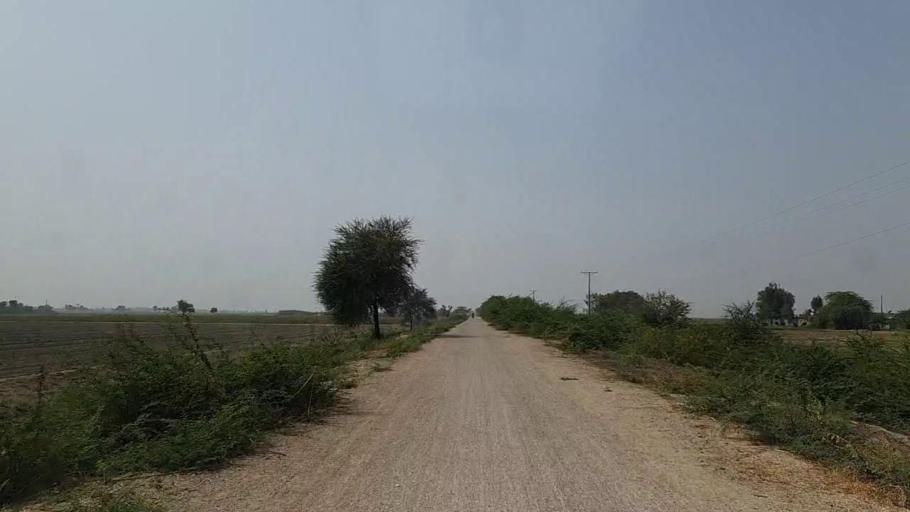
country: PK
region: Sindh
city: Naukot
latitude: 24.7952
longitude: 69.3609
